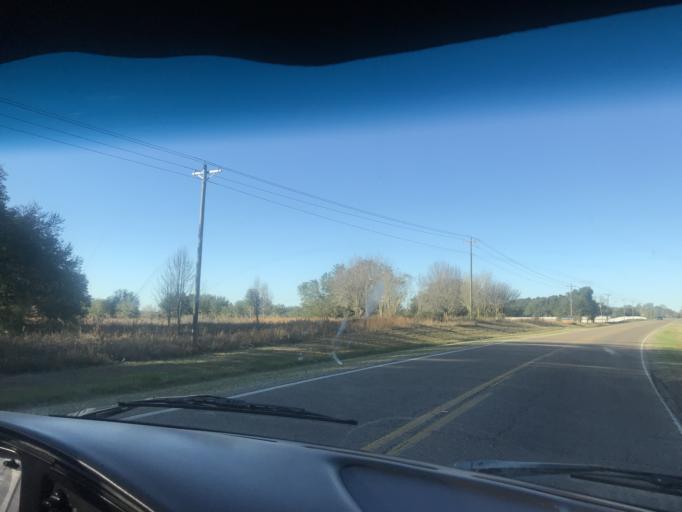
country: US
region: Louisiana
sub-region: Washington Parish
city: Franklinton
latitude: 30.6600
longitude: -90.2035
